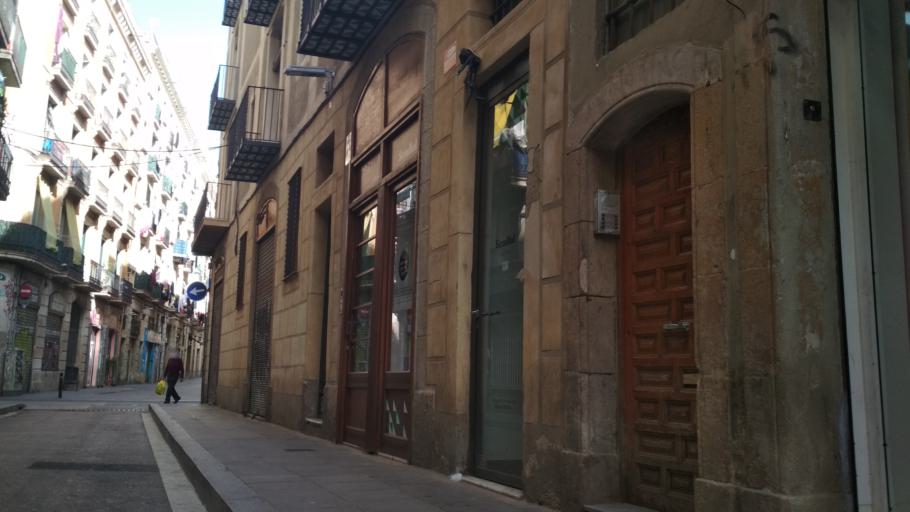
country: ES
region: Catalonia
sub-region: Provincia de Barcelona
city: Ciutat Vella
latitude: 41.3780
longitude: 2.1714
